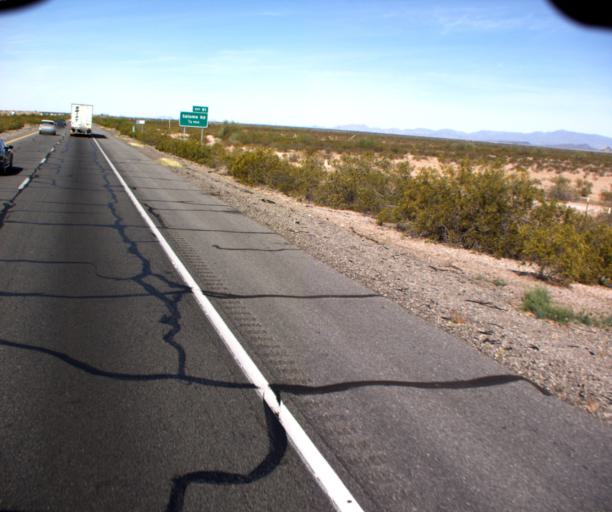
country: US
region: Arizona
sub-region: La Paz County
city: Salome
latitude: 33.5348
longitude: -113.1411
